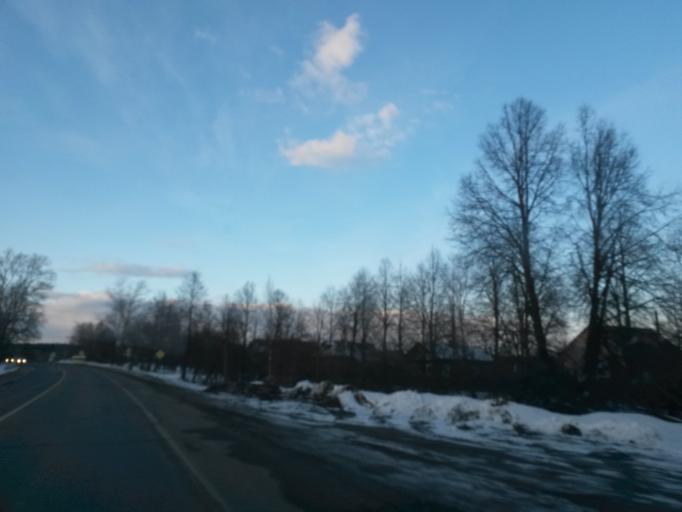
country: RU
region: Jaroslavl
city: Pereslavl'-Zalesskiy
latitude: 56.6523
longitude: 38.6987
